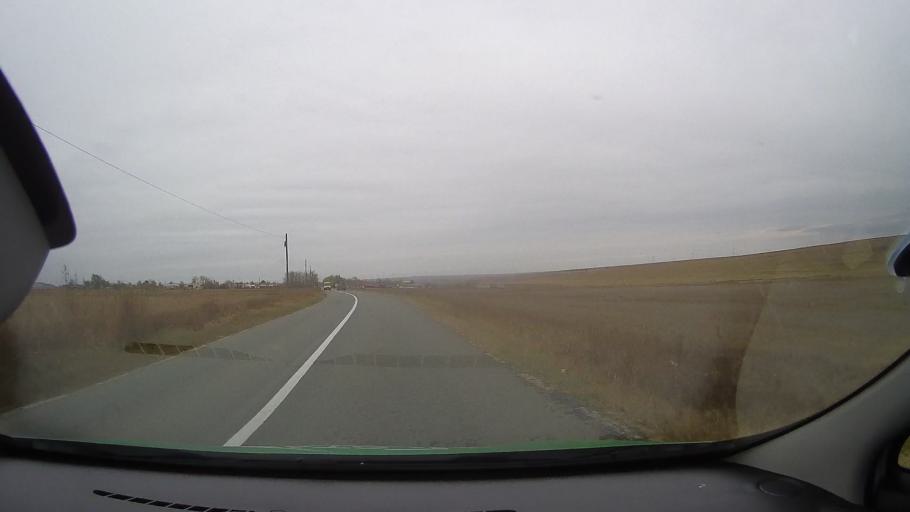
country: RO
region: Constanta
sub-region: Comuna Silistea
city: Silistea
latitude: 44.4387
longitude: 28.2280
